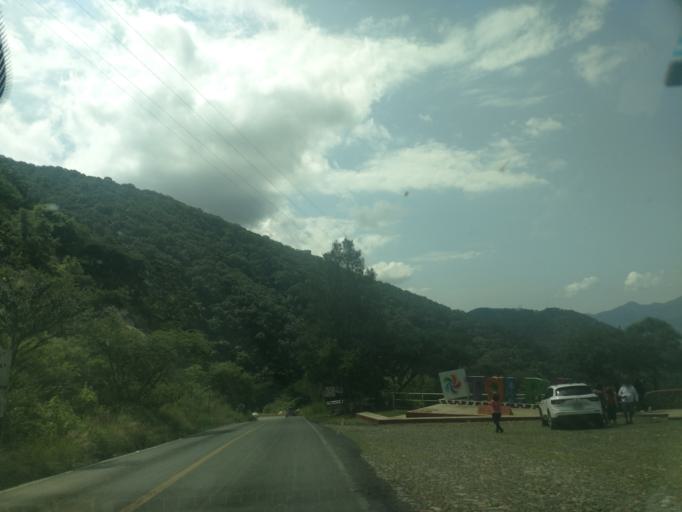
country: MX
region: Jalisco
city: Talpa de Allende
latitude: 20.4201
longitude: -104.8005
